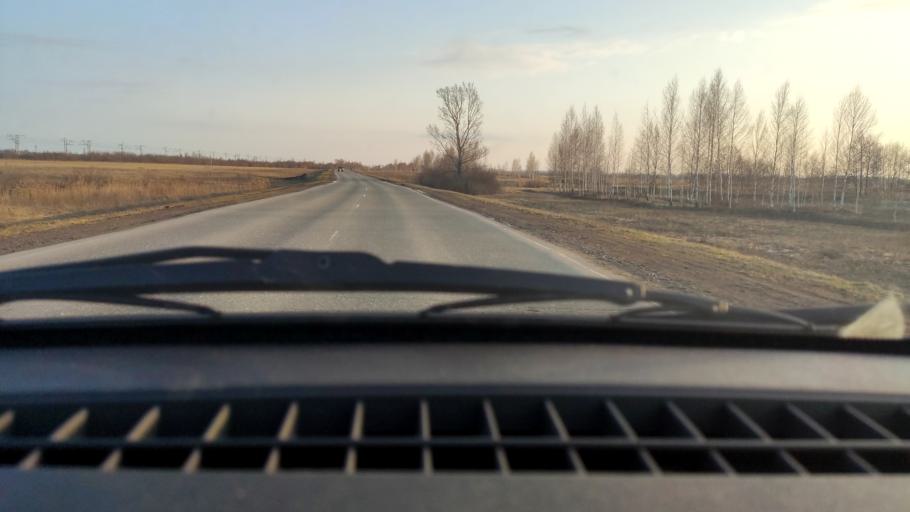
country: RU
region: Bashkortostan
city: Chishmy
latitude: 54.4349
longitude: 55.2359
